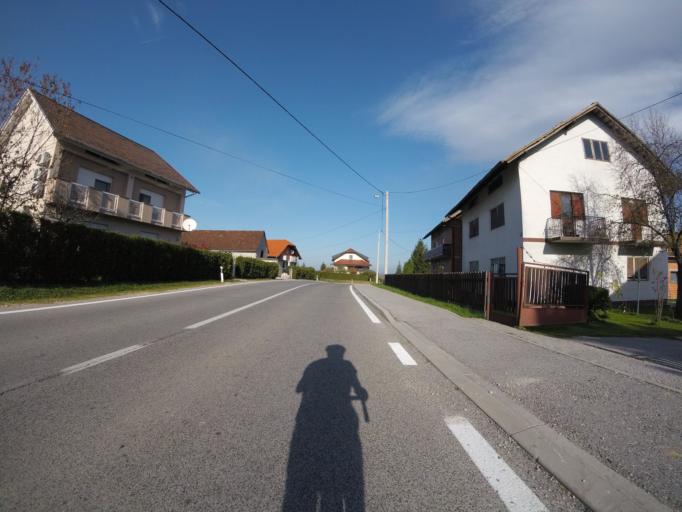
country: HR
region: Zagrebacka
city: Mraclin
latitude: 45.6364
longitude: 16.0540
